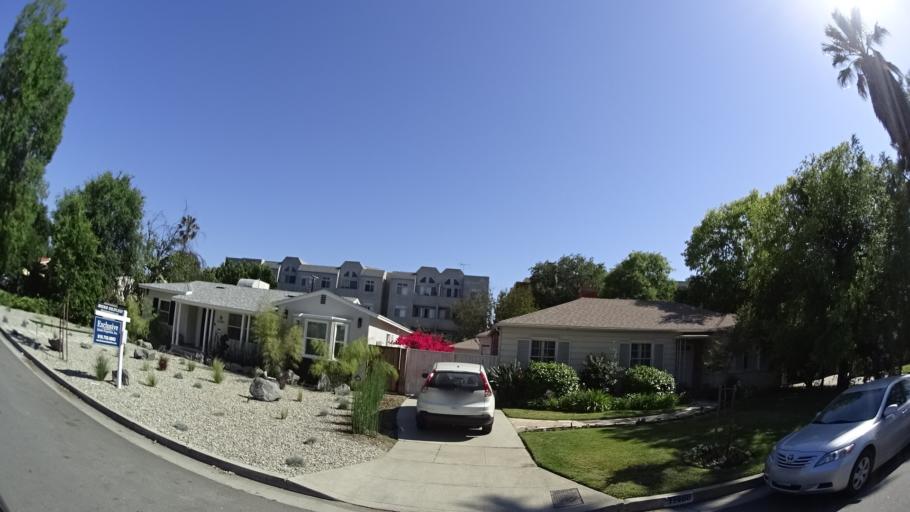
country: US
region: California
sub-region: Los Angeles County
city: North Hollywood
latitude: 34.1586
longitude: -118.3818
